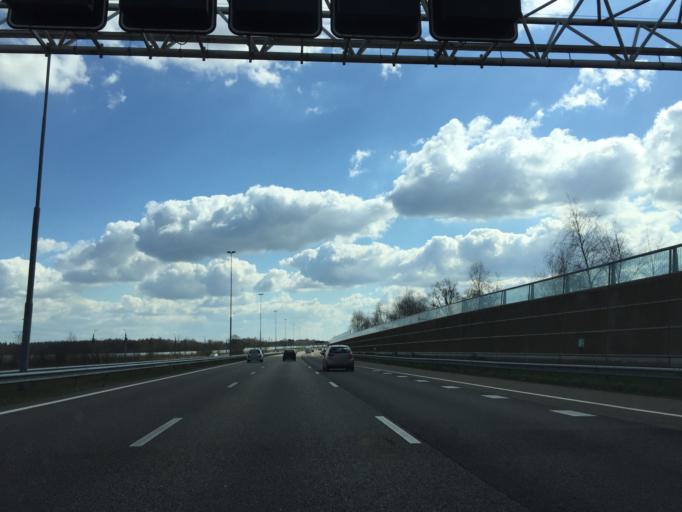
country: NL
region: North Brabant
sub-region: Gemeente Breda
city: Breda
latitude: 51.5570
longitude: 4.7367
